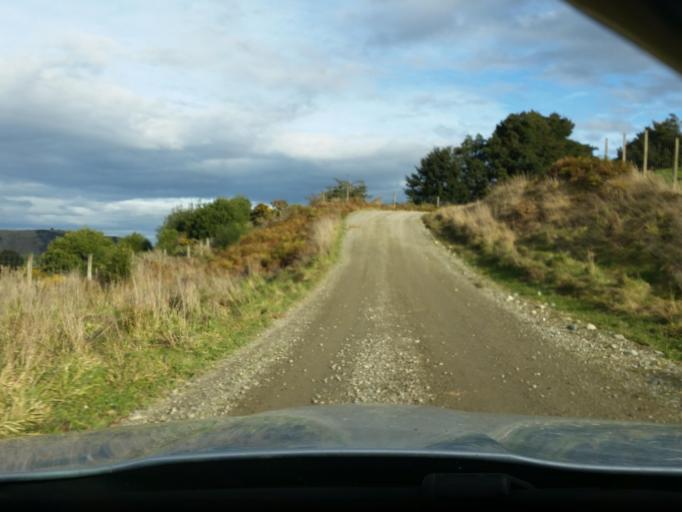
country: NZ
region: Southland
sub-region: Southland District
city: Te Anau
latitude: -45.8053
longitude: 167.6379
